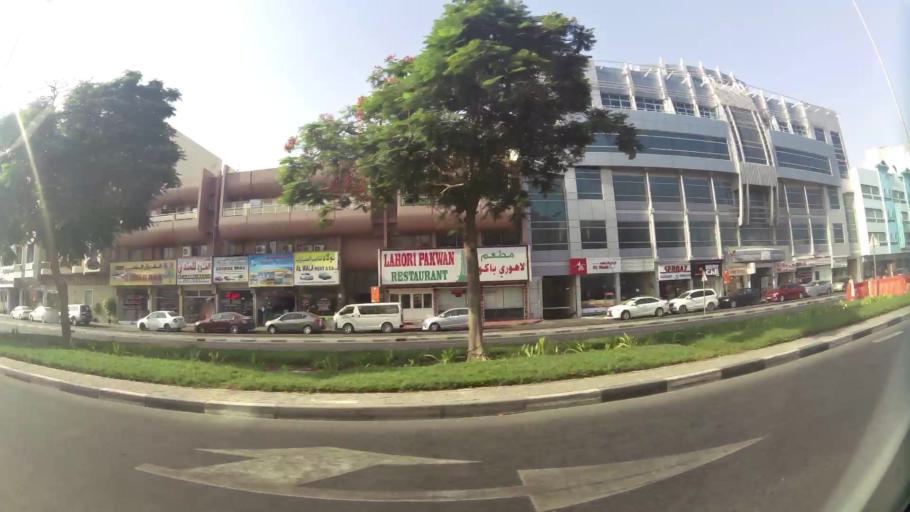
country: AE
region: Ash Shariqah
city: Sharjah
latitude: 25.2790
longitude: 55.3133
